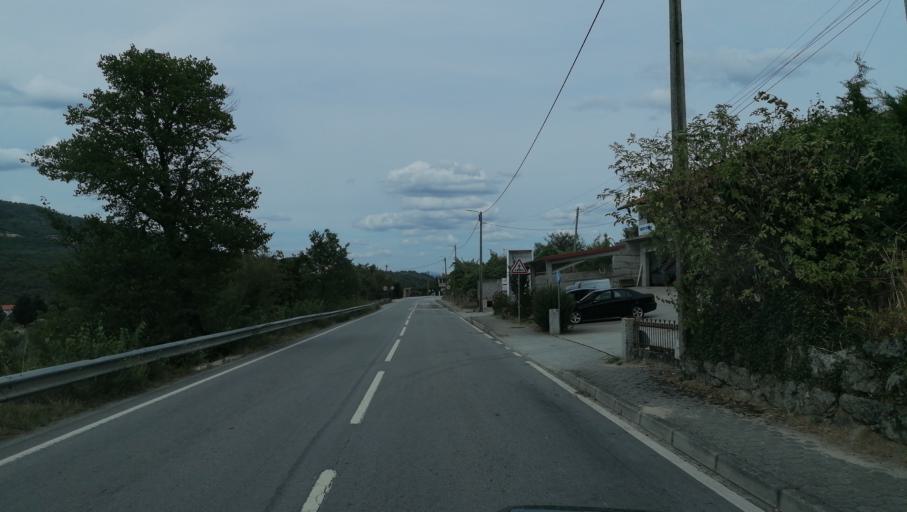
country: PT
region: Vila Real
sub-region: Vila Pouca de Aguiar
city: Vila Pouca de Aguiar
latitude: 41.5276
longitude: -7.6124
